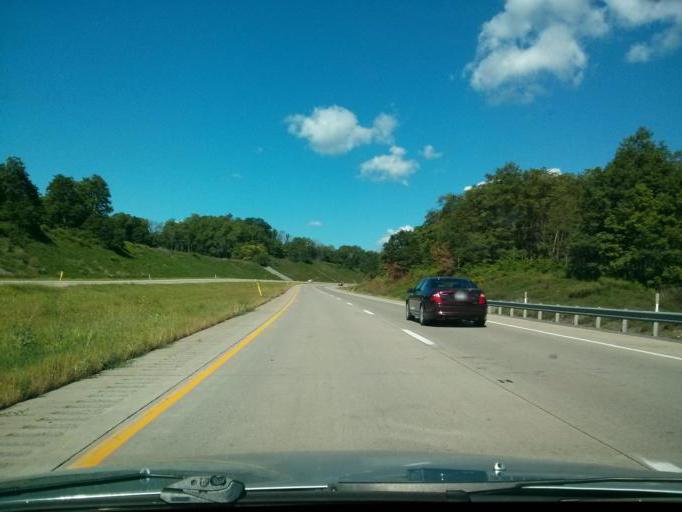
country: US
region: Pennsylvania
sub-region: Centre County
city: Park Forest Village
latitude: 40.8240
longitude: -77.9490
